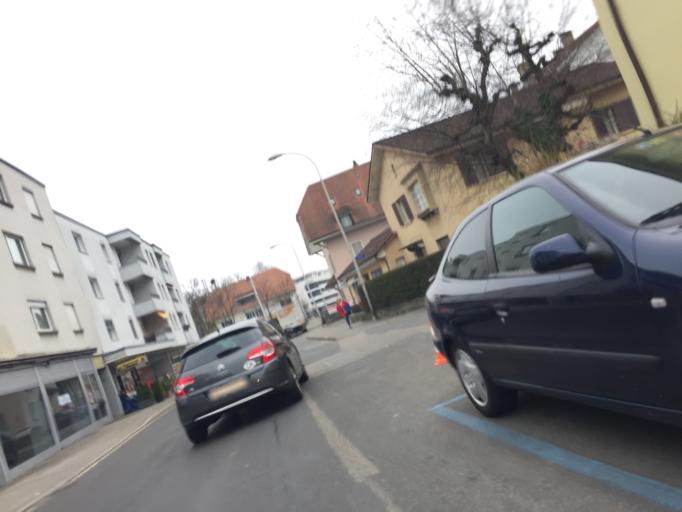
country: CH
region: Bern
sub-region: Bern-Mittelland District
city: Koniz
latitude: 46.9389
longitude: 7.3887
